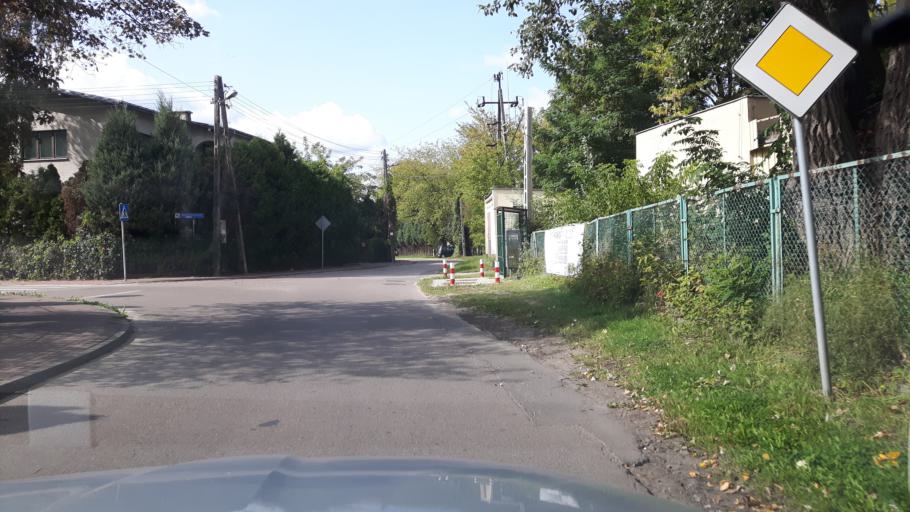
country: PL
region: Masovian Voivodeship
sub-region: Powiat legionowski
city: Nieporet
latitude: 52.4555
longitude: 21.0132
